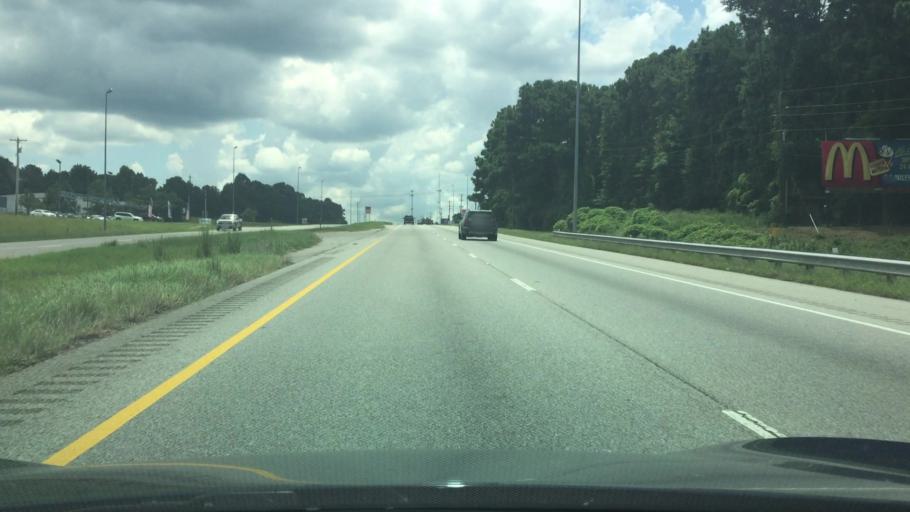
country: US
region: Alabama
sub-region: Pike County
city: Troy
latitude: 31.8150
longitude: -85.9922
